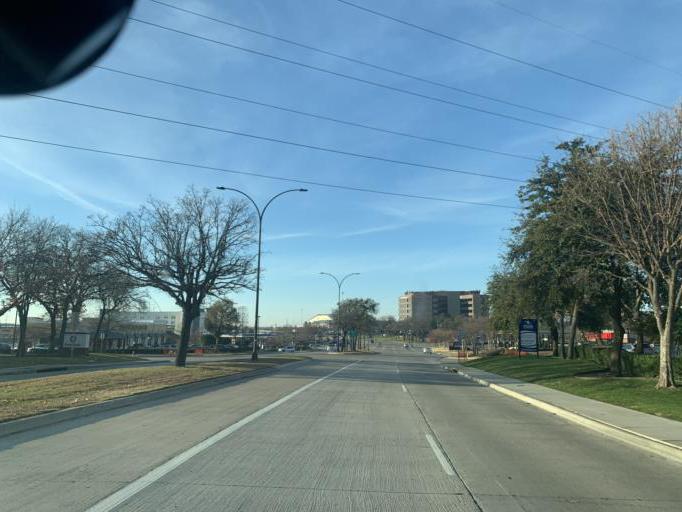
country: US
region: Texas
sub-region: Tarrant County
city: Arlington
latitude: 32.7646
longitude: -97.0742
